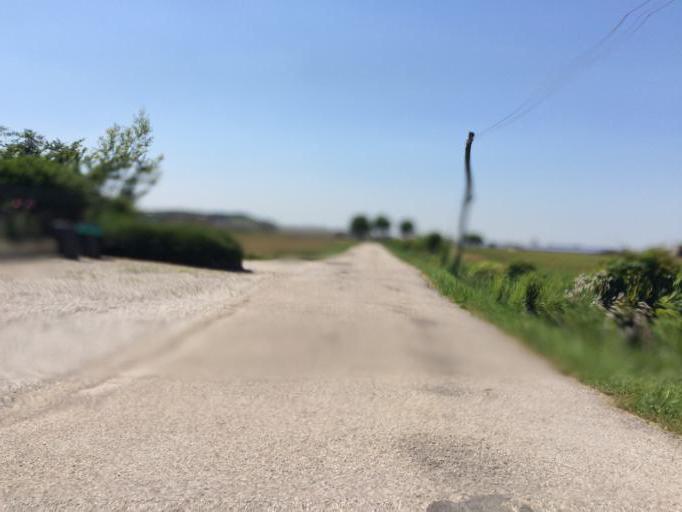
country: IT
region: Veneto
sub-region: Provincia di Vicenza
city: Ponte di Nanto
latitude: 45.4169
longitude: 11.5955
